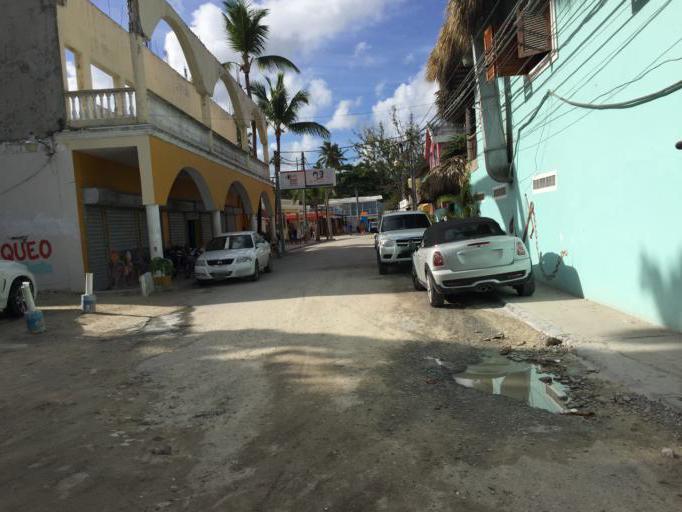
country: DO
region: San Juan
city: Punta Cana
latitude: 18.6919
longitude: -68.4227
